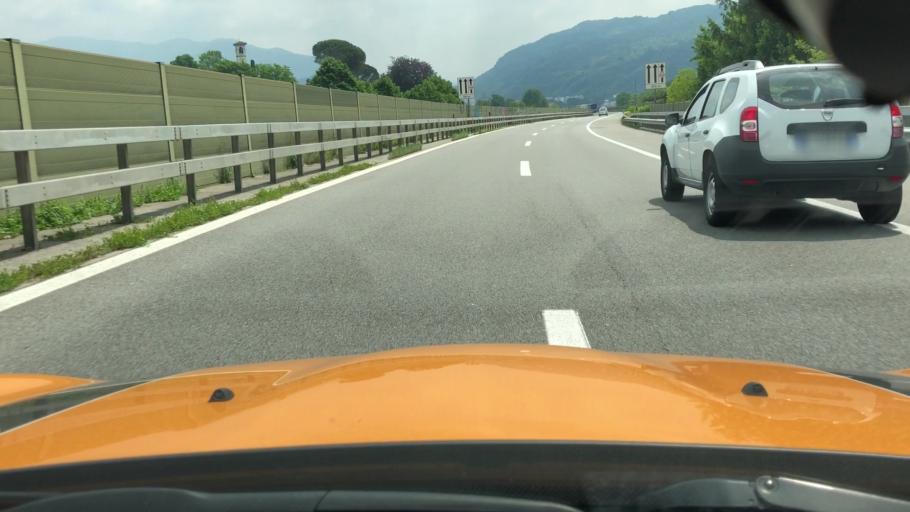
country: CH
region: Ticino
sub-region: Mendrisio District
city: Balerna
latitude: 45.8460
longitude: 8.9951
